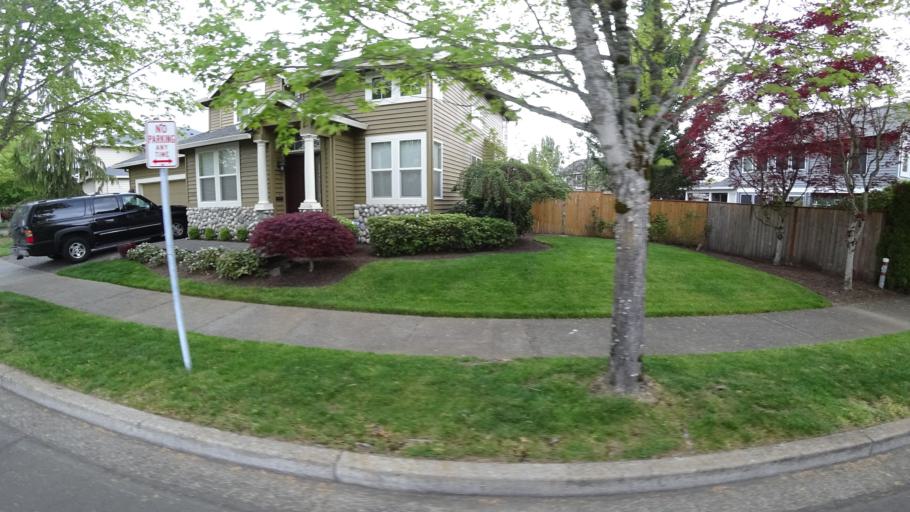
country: US
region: Oregon
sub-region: Washington County
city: Hillsboro
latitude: 45.5445
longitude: -122.9726
